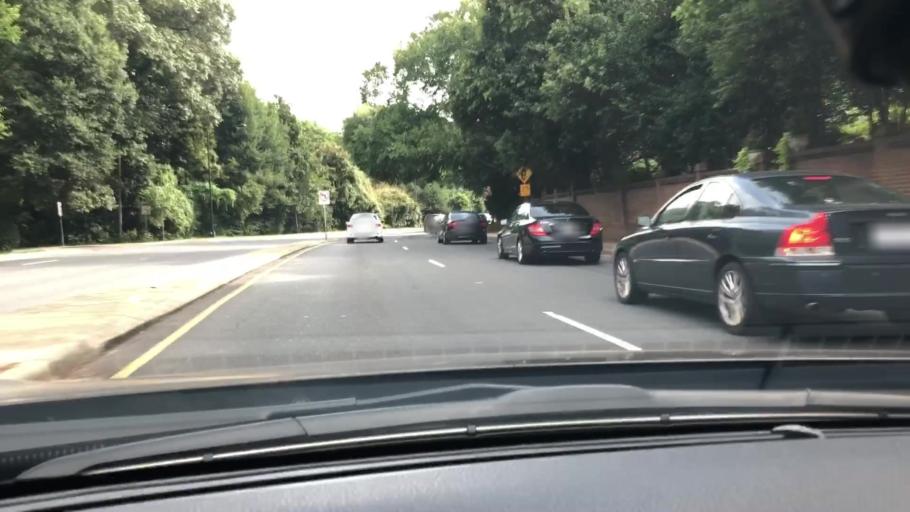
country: US
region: North Carolina
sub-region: Mecklenburg County
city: Charlotte
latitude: 35.1599
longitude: -80.8211
